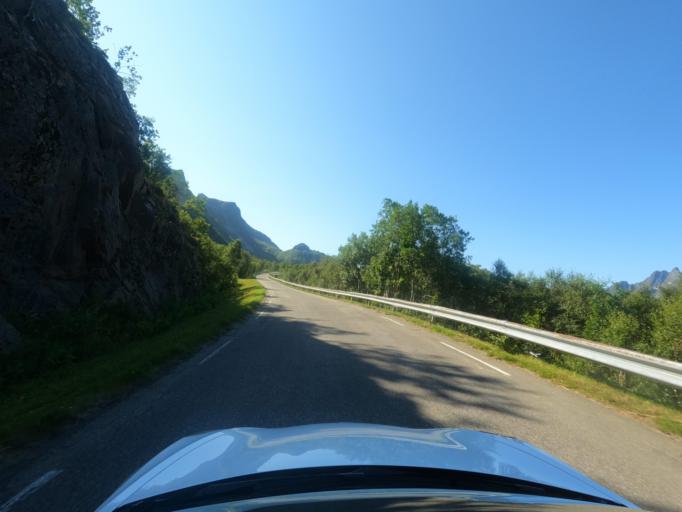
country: NO
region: Nordland
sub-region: Hadsel
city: Stokmarknes
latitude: 68.3530
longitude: 15.0684
